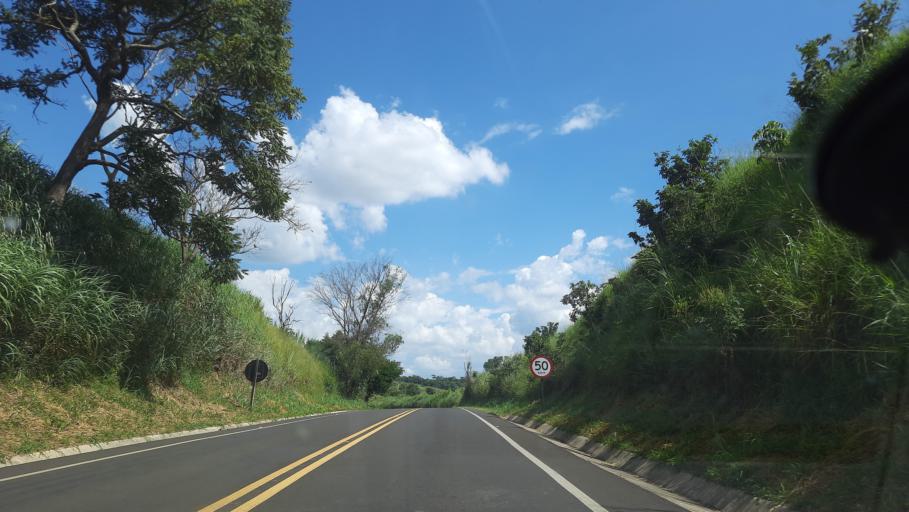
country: BR
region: Sao Paulo
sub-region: Sao Jose Do Rio Pardo
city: Sao Jose do Rio Pardo
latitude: -21.6032
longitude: -46.9382
